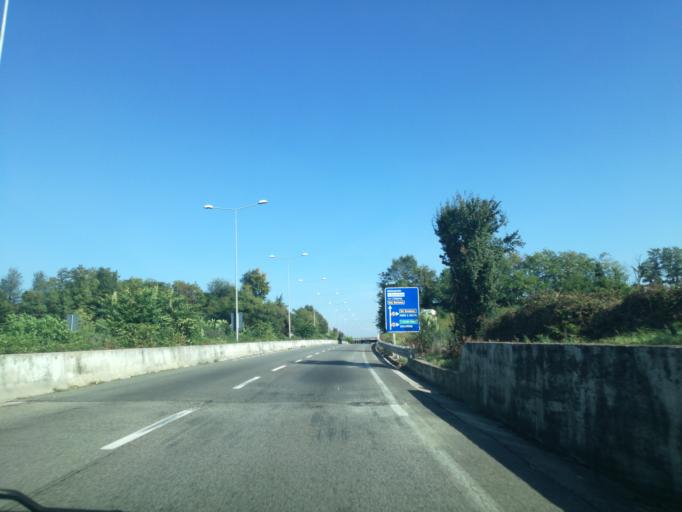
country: IT
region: Lombardy
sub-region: Provincia di Bergamo
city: Ghiaie
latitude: 45.6775
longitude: 9.5956
